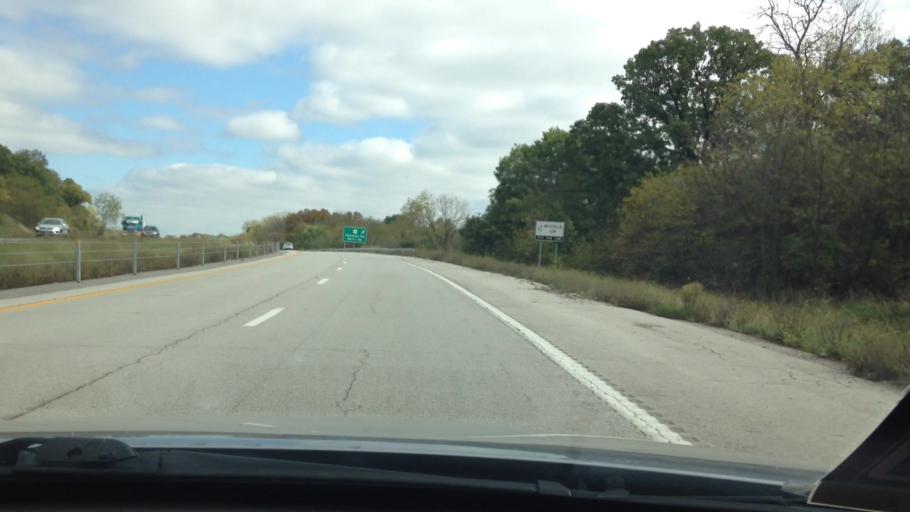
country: US
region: Missouri
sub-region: Platte County
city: Weatherby Lake
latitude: 39.2450
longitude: -94.7429
